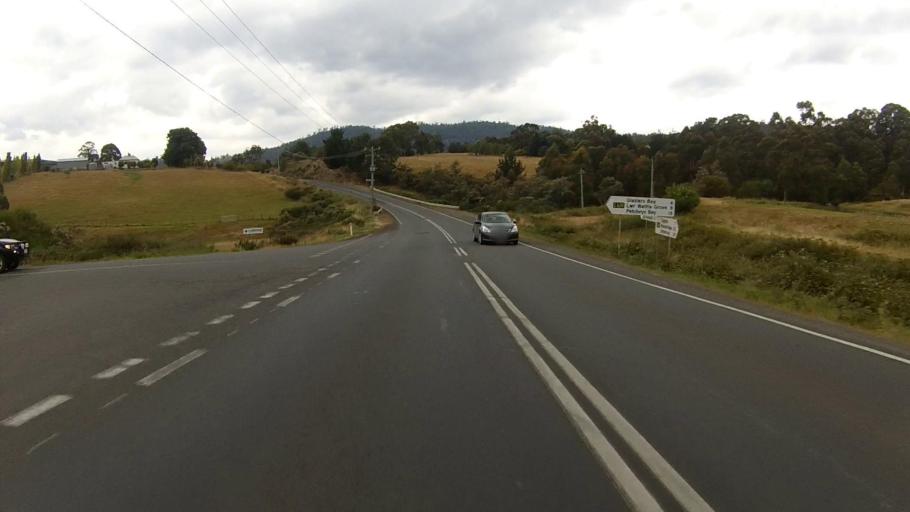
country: AU
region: Tasmania
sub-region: Huon Valley
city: Franklin
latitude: -43.1145
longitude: 147.0360
